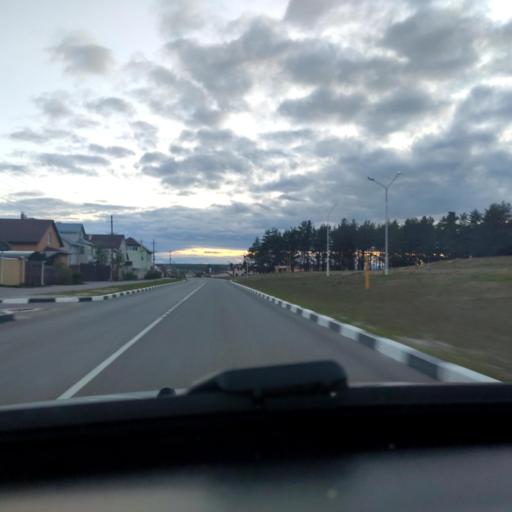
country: RU
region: Voronezj
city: Kolodeznyy
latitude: 51.3264
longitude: 39.2024
